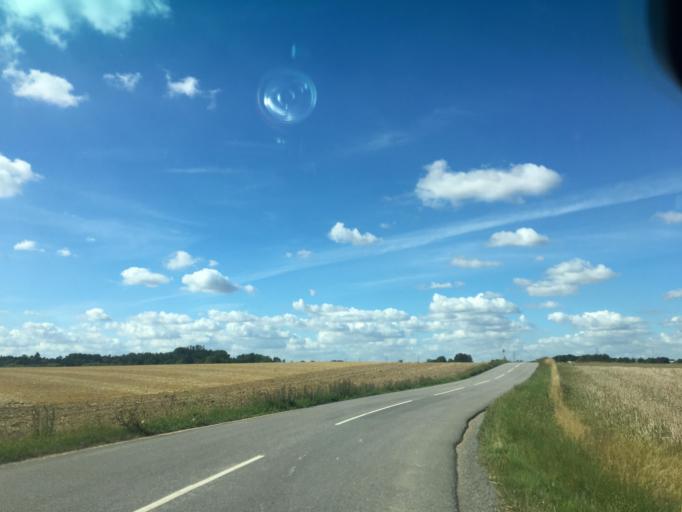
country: DK
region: Zealand
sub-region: Solrod Kommune
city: Solrod Strand
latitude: 55.5695
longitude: 12.2126
